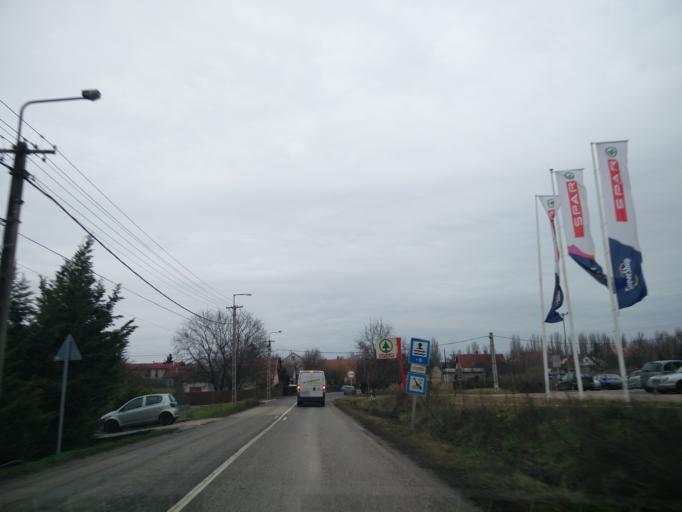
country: HU
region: Pest
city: Gyomro
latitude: 47.4150
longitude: 19.4033
